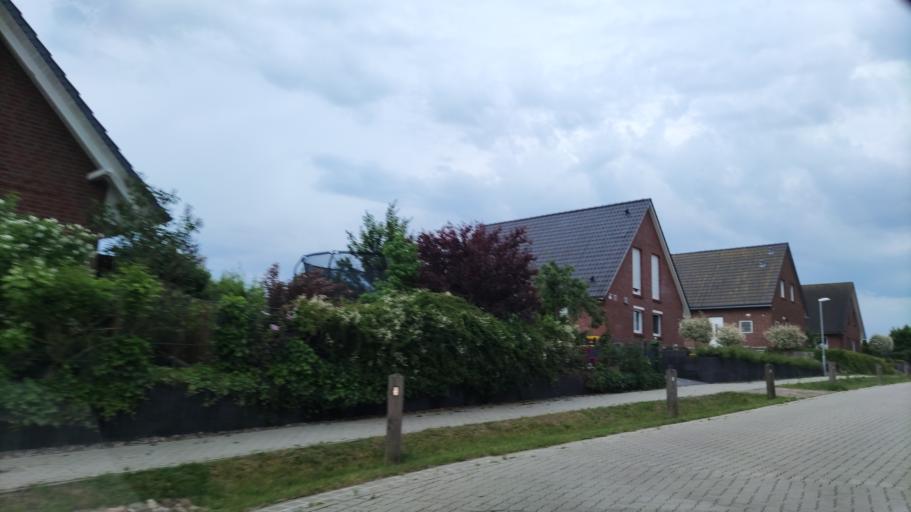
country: DE
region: Lower Saxony
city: Reinstorf
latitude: 53.2728
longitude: 10.5681
